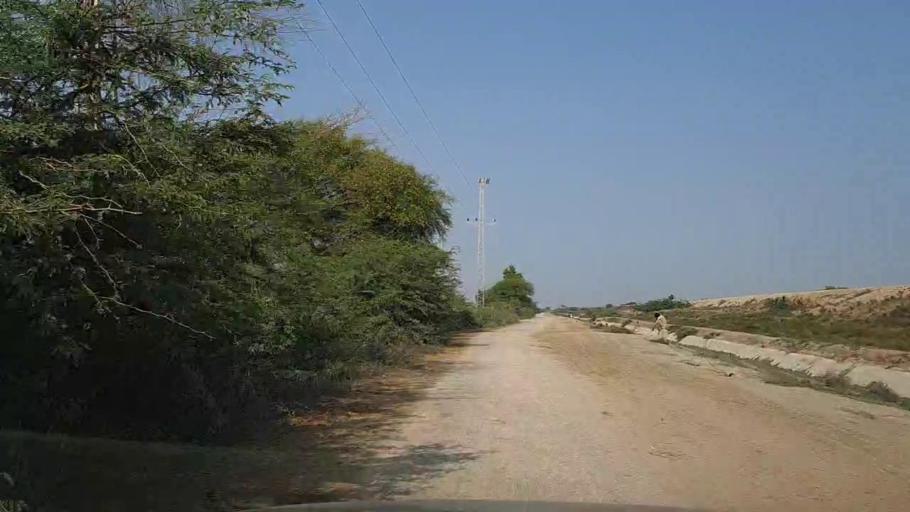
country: PK
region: Sindh
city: Chuhar Jamali
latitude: 24.5138
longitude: 67.9248
